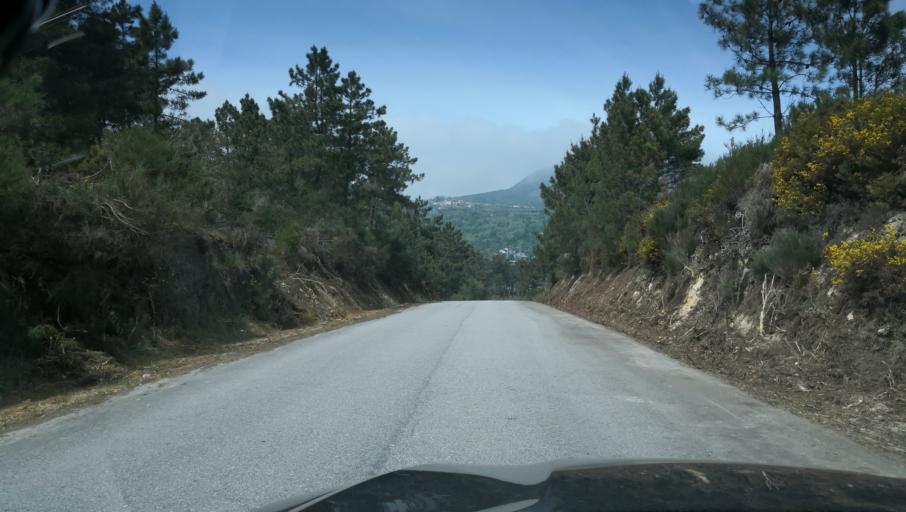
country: PT
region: Vila Real
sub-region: Vila Real
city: Vila Real
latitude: 41.2804
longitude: -7.8025
